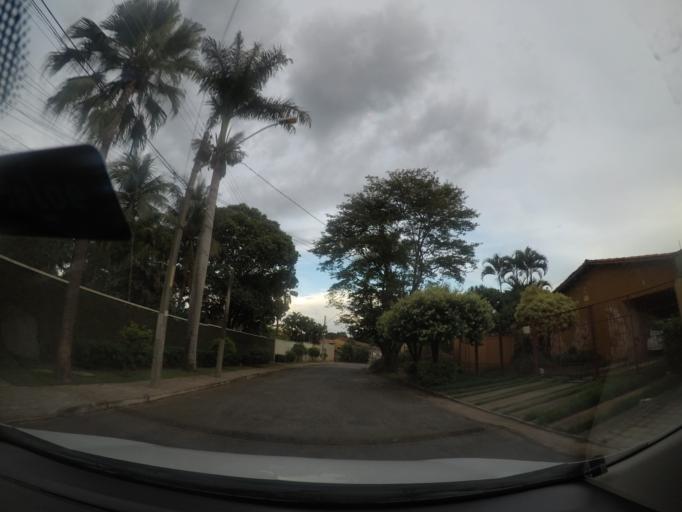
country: BR
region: Goias
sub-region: Goiania
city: Goiania
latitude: -16.6529
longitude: -49.2317
